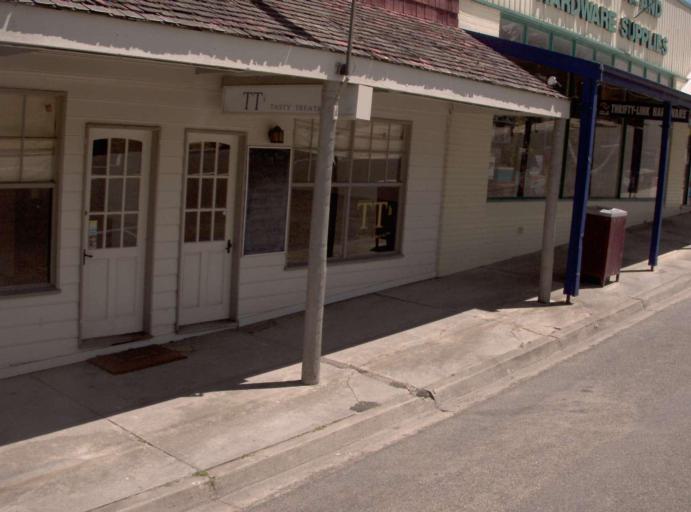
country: AU
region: Victoria
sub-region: Alpine
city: Mount Beauty
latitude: -37.0999
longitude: 147.5930
